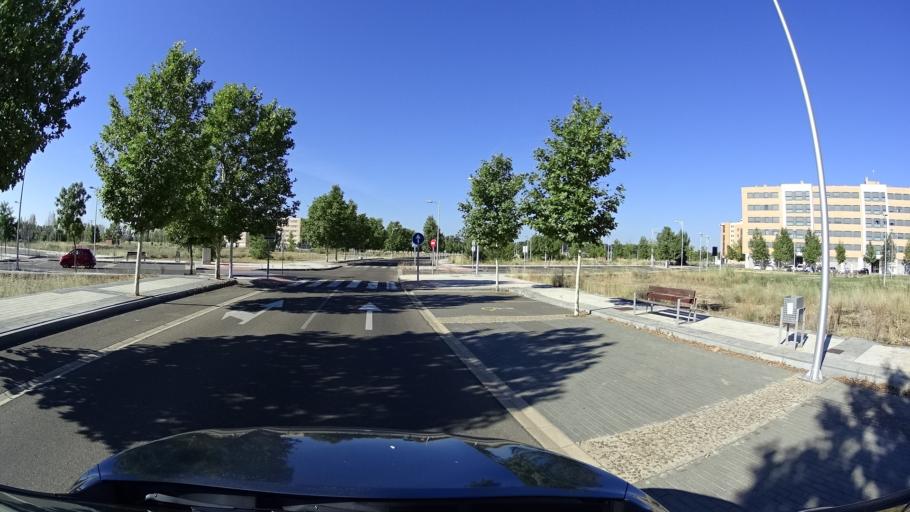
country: ES
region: Castille and Leon
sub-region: Provincia de Leon
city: Leon
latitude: 42.5822
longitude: -5.5606
